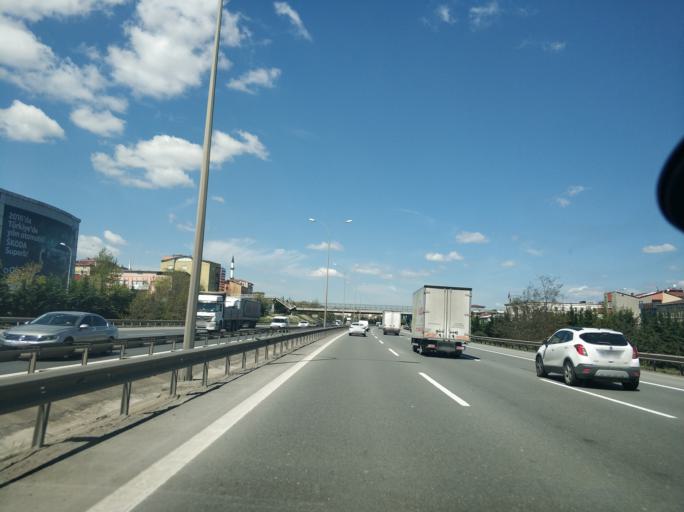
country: TR
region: Istanbul
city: Sultanbeyli
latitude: 40.9608
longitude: 29.2819
